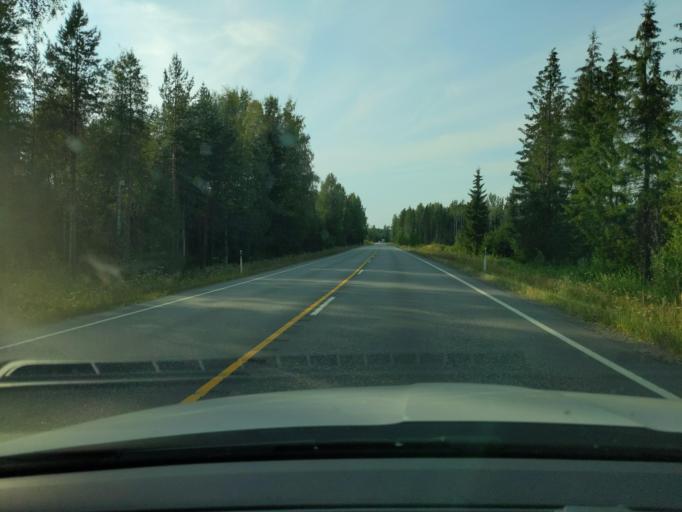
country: FI
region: Paijanne Tavastia
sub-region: Lahti
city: Padasjoki
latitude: 61.3172
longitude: 25.2874
